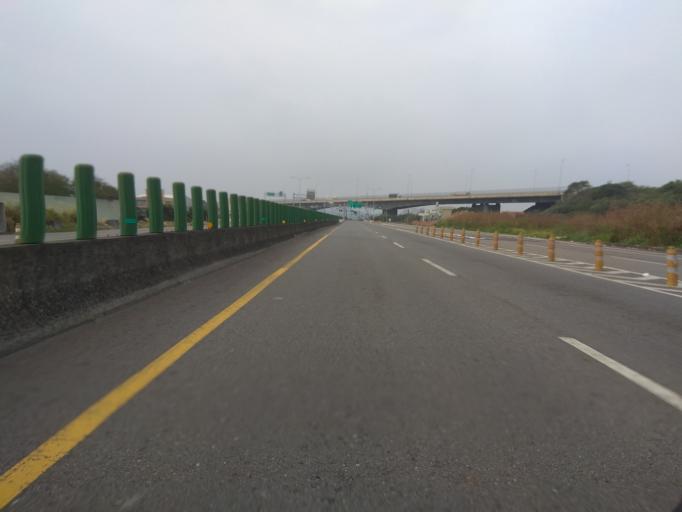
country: TW
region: Taiwan
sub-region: Miaoli
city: Miaoli
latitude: 24.6835
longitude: 120.8498
